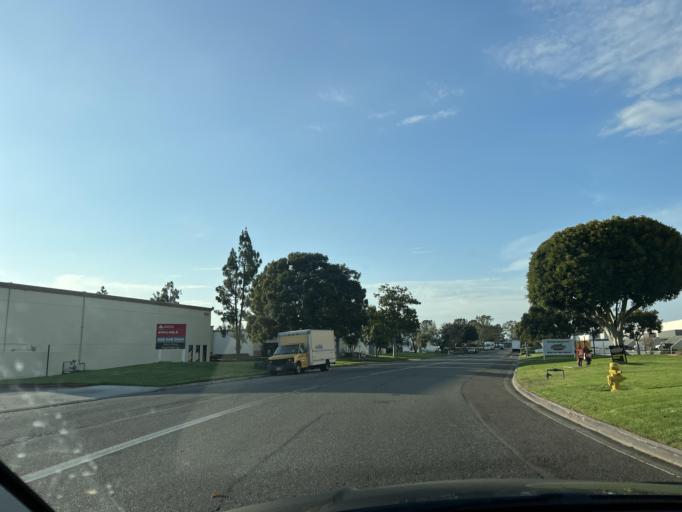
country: US
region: California
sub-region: San Diego County
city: Fairbanks Ranch
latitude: 32.8914
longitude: -117.1440
